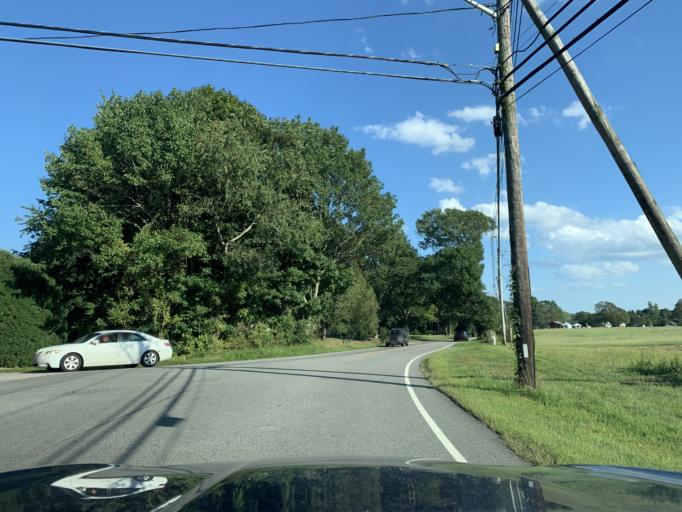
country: US
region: Rhode Island
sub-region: Washington County
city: North Kingstown
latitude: 41.5405
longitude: -71.5006
